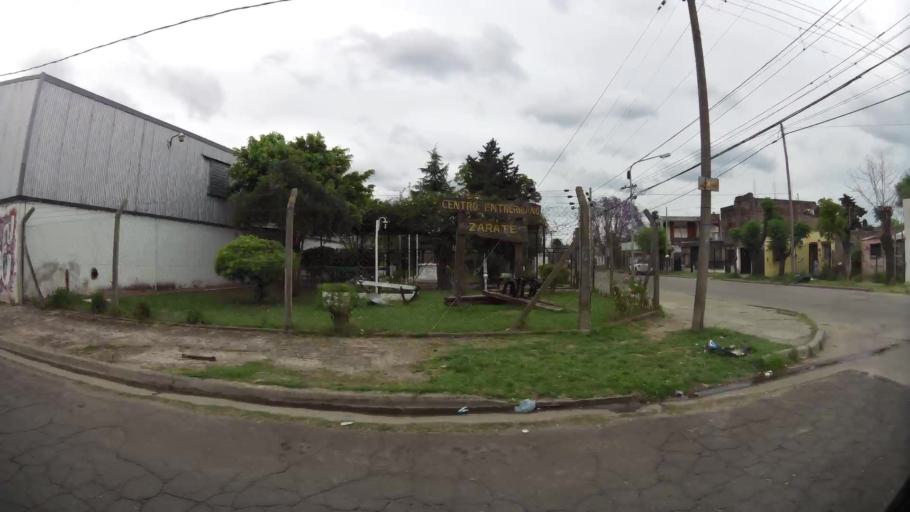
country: AR
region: Buenos Aires
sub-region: Partido de Zarate
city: Zarate
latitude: -34.1143
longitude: -59.0176
